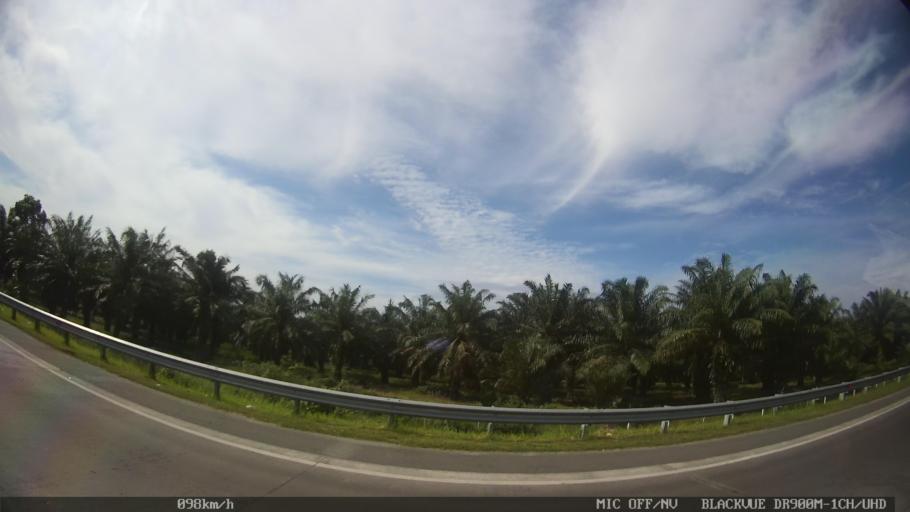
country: ID
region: North Sumatra
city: Sunggal
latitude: 3.6384
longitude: 98.6162
